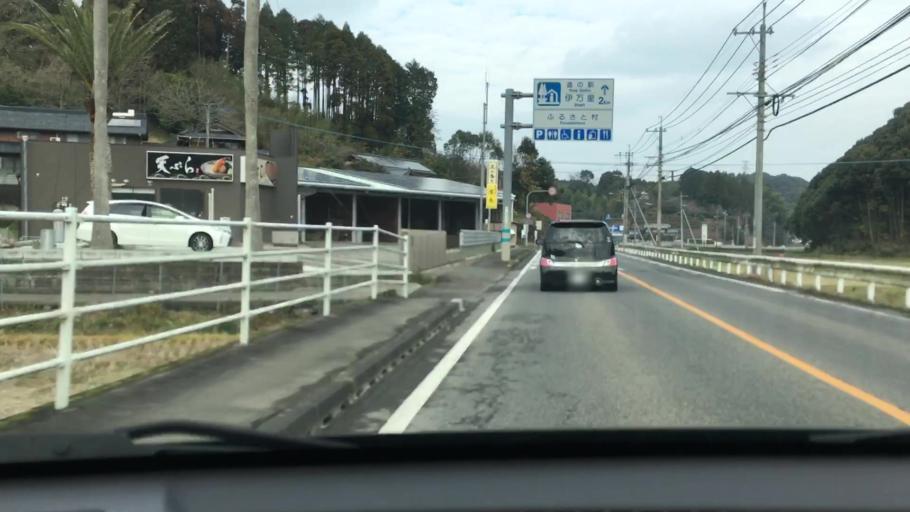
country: JP
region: Saga Prefecture
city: Imaricho-ko
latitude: 33.2990
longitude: 129.9176
